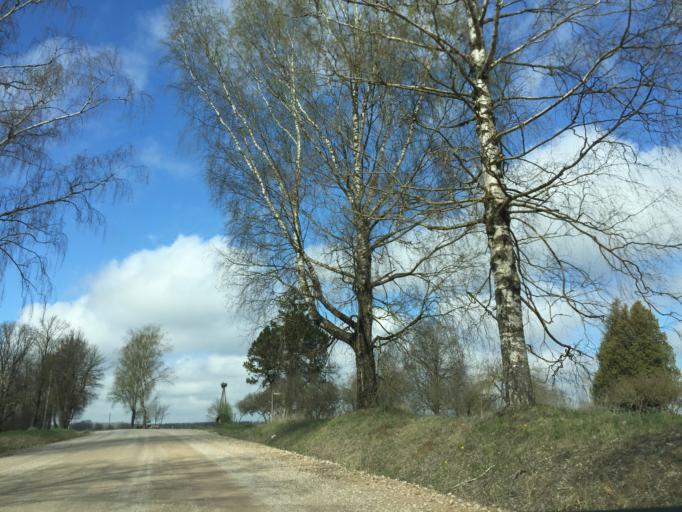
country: LV
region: Apes Novads
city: Ape
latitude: 57.4796
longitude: 26.4603
